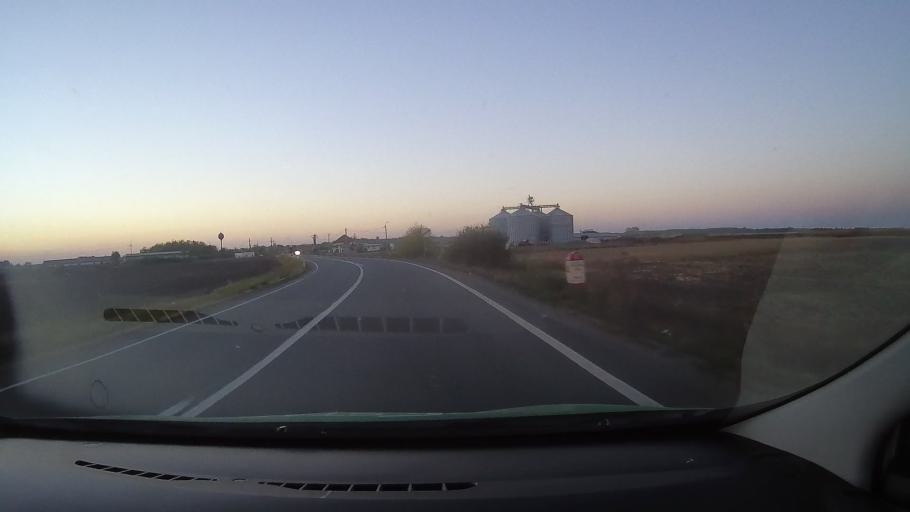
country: RO
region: Bihor
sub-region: Comuna Tarcea
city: Tarcea
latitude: 47.4515
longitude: 22.1837
